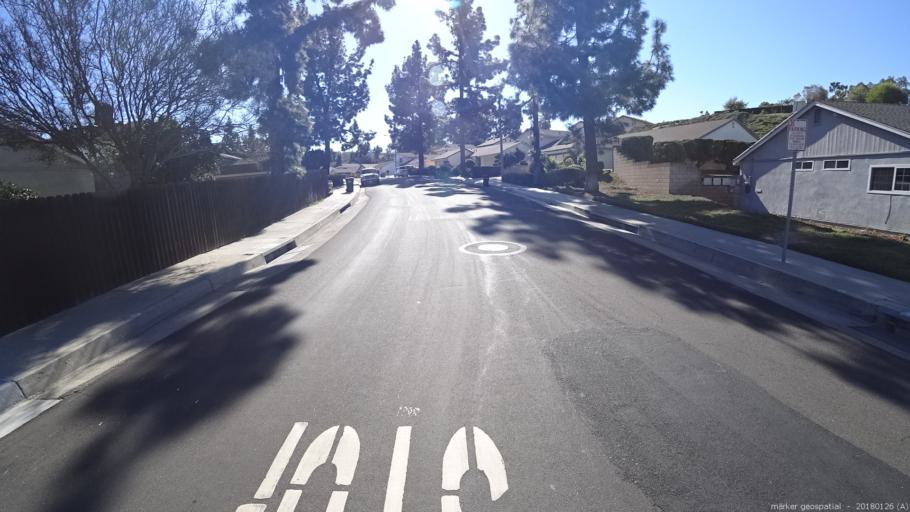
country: US
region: California
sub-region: Los Angeles County
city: Walnut
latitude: 33.9964
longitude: -117.8626
